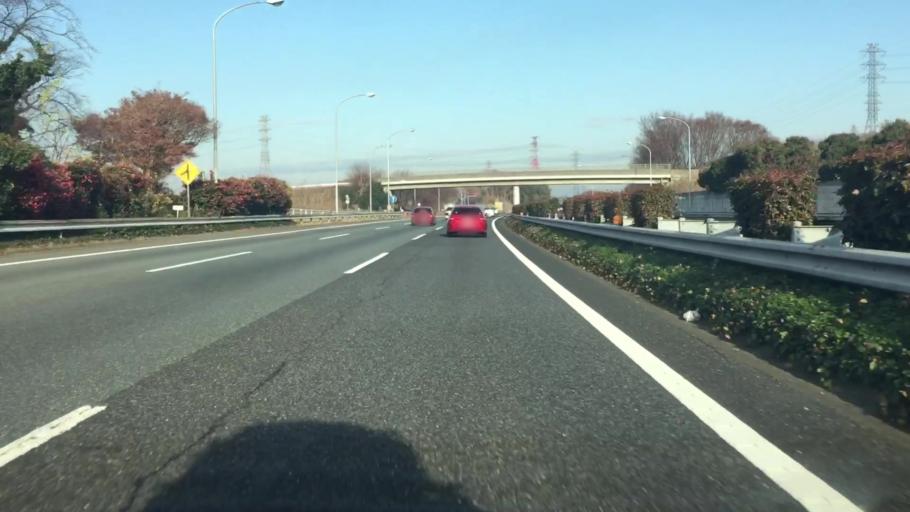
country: JP
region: Saitama
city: Yorii
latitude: 36.1719
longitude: 139.1944
